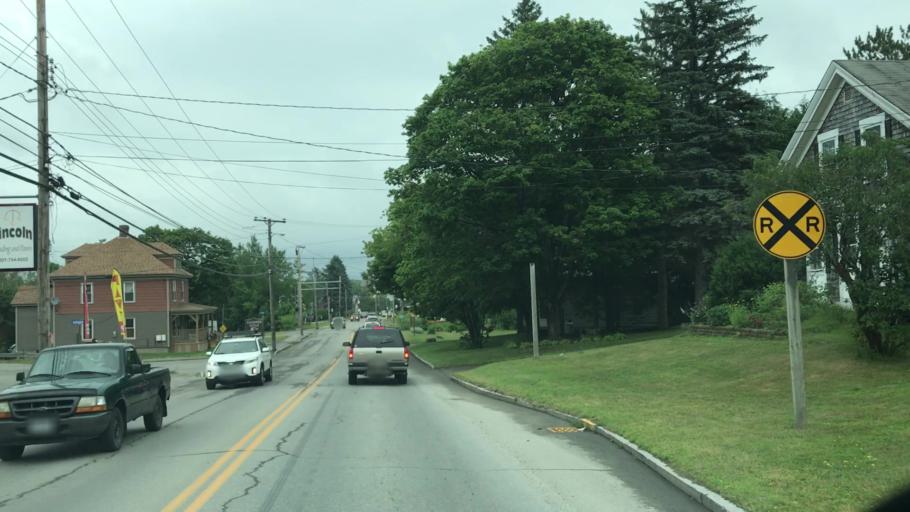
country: US
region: Maine
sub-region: Penobscot County
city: Lincoln
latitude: 45.3631
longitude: -68.5104
